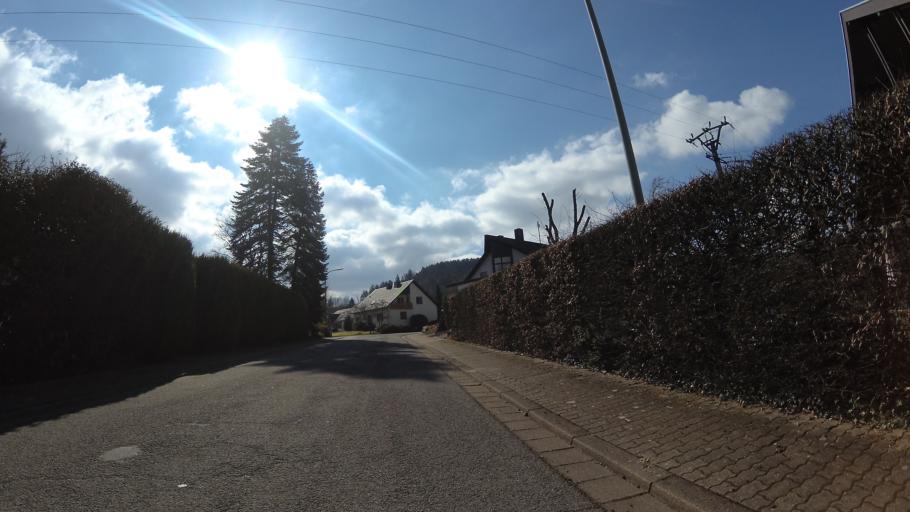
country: DE
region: Saarland
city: Merzig
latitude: 49.4029
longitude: 6.6453
